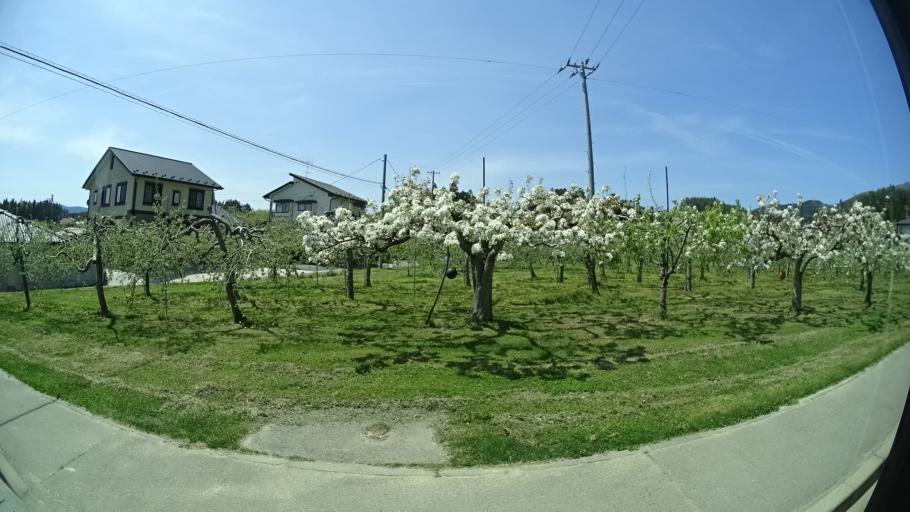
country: JP
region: Iwate
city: Ofunato
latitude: 39.0217
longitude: 141.6477
